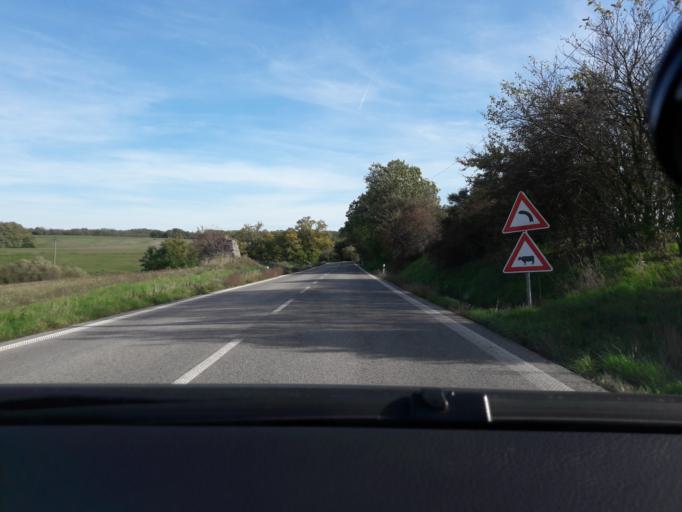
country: SK
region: Banskobystricky
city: Dudince
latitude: 48.2576
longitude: 18.7586
